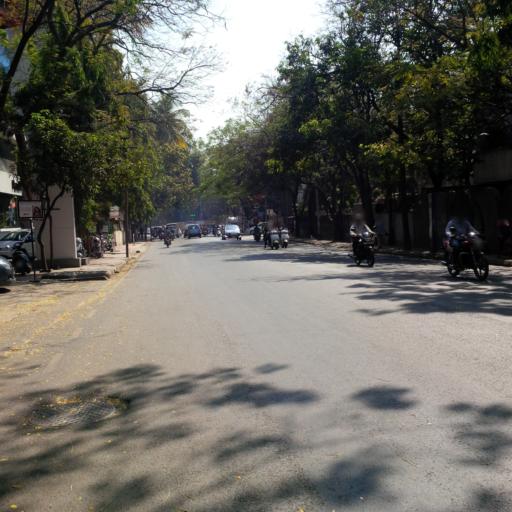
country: IN
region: Maharashtra
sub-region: Pune Division
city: Pune
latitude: 18.5118
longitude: 73.8290
